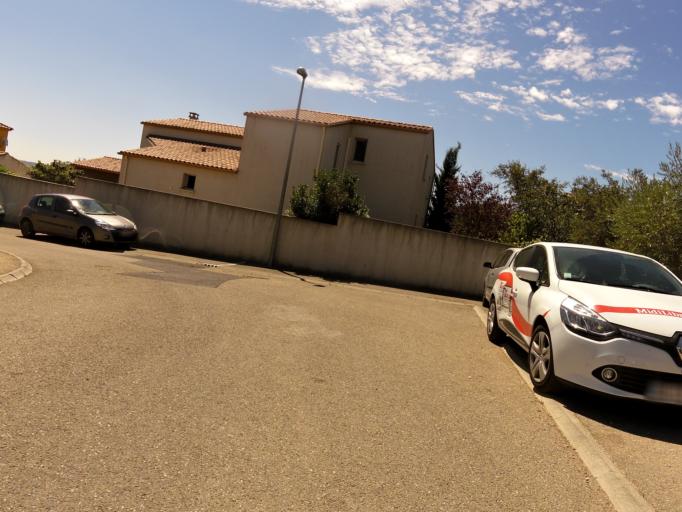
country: FR
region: Languedoc-Roussillon
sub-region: Departement du Gard
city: Vergeze
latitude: 43.7455
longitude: 4.2299
